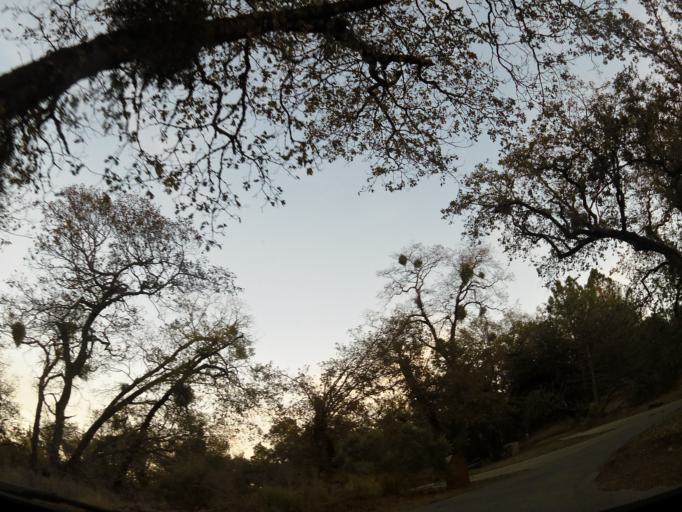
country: US
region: California
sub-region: San Benito County
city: San Juan Bautista
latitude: 36.7604
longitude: -121.5047
